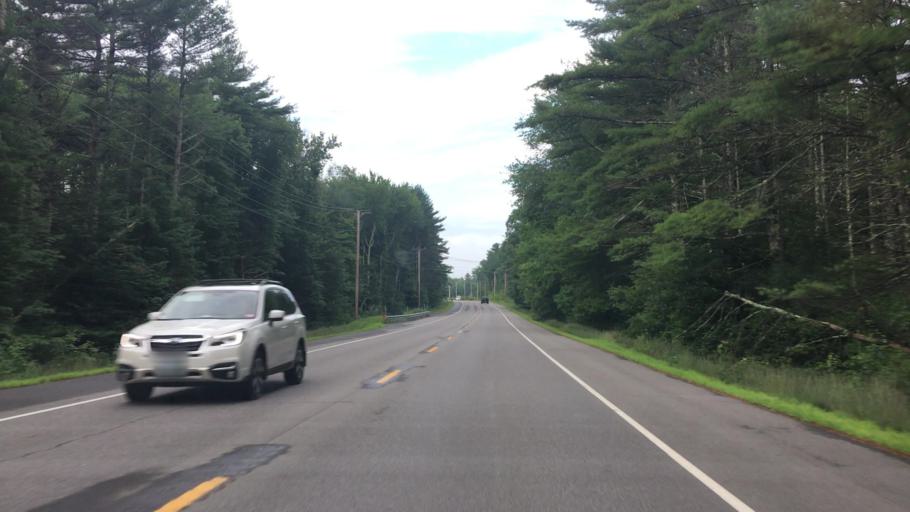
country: US
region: Maine
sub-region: York County
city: Lebanon
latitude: 43.3656
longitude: -70.9038
